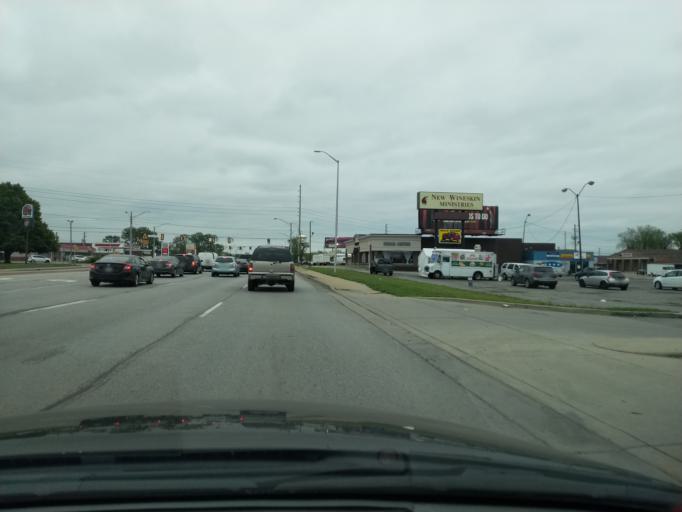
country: US
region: Indiana
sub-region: Marion County
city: Speedway
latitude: 39.8239
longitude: -86.2367
